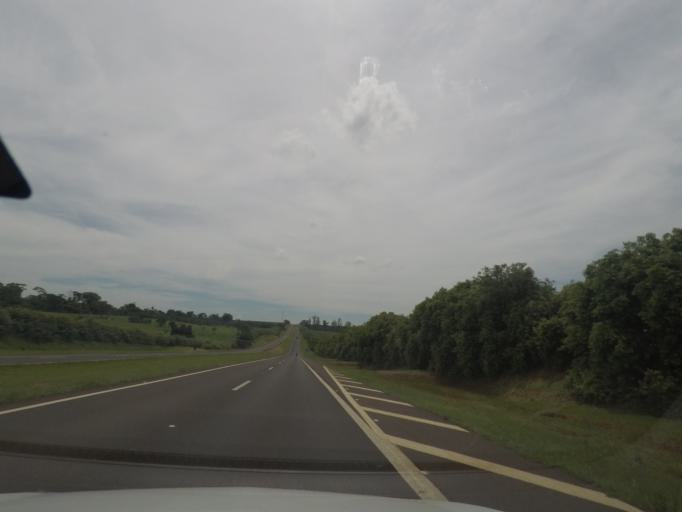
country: BR
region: Sao Paulo
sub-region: Bebedouro
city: Bebedouro
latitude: -21.0046
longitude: -48.4291
